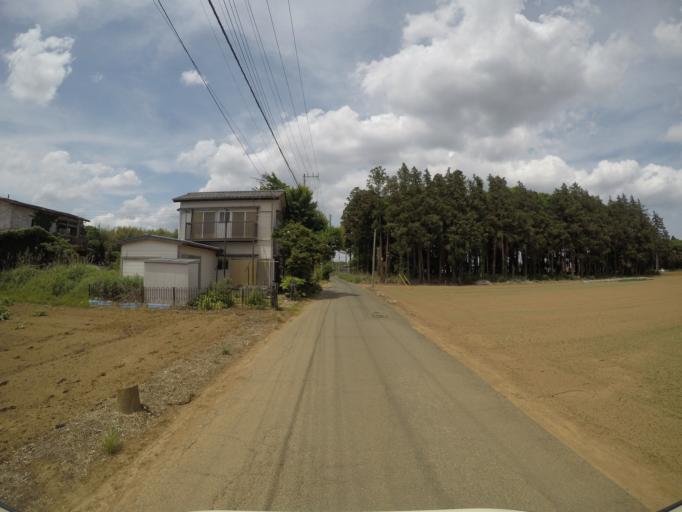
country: JP
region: Ibaraki
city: Ushiku
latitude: 35.9821
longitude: 140.1156
